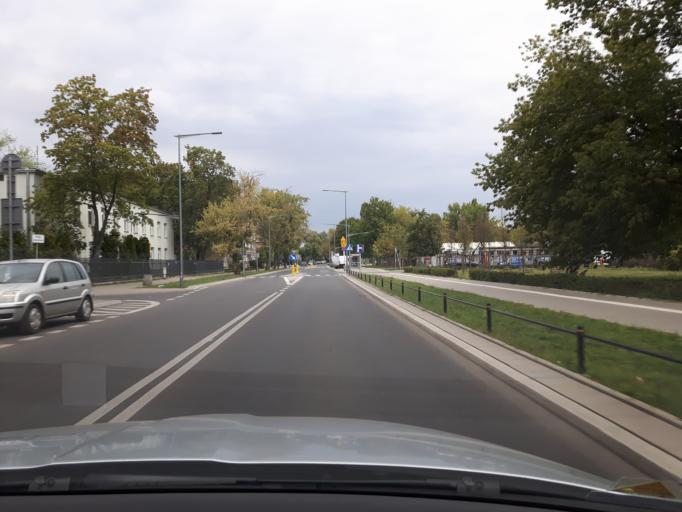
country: PL
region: Masovian Voivodeship
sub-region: Warszawa
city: Praga Polnoc
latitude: 52.2634
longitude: 21.0339
